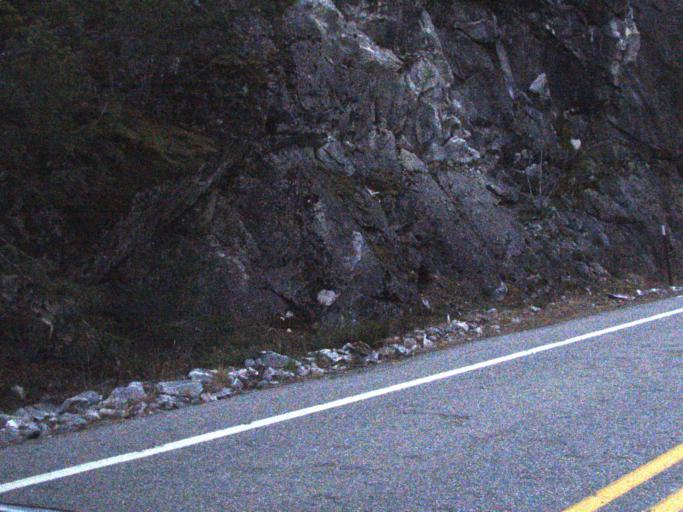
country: US
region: Washington
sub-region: Snohomish County
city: Darrington
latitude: 48.6950
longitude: -121.2196
